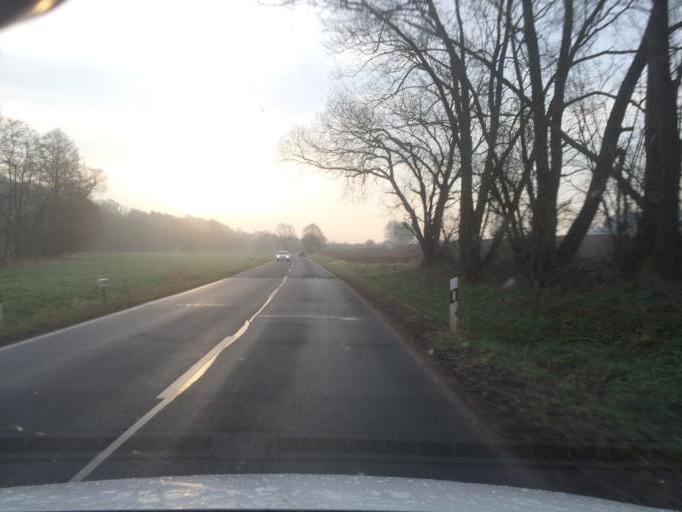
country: DE
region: Thuringia
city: Weissenborn-Luderode
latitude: 51.5376
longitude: 10.3991
